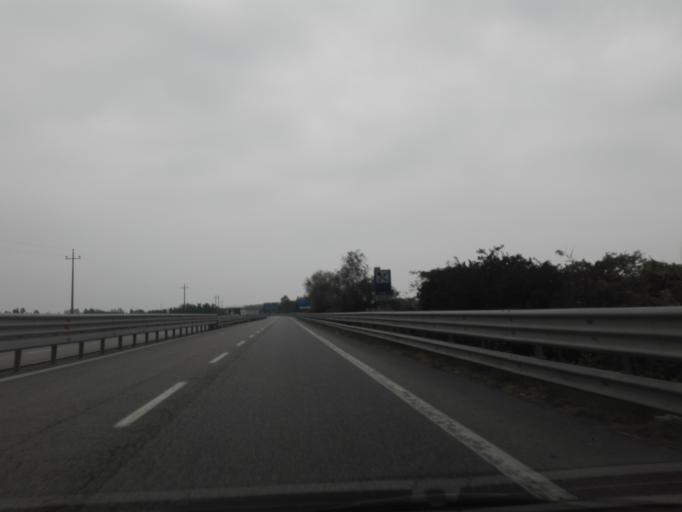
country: IT
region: Veneto
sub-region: Provincia di Verona
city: Oppeano
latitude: 45.2933
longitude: 11.1740
